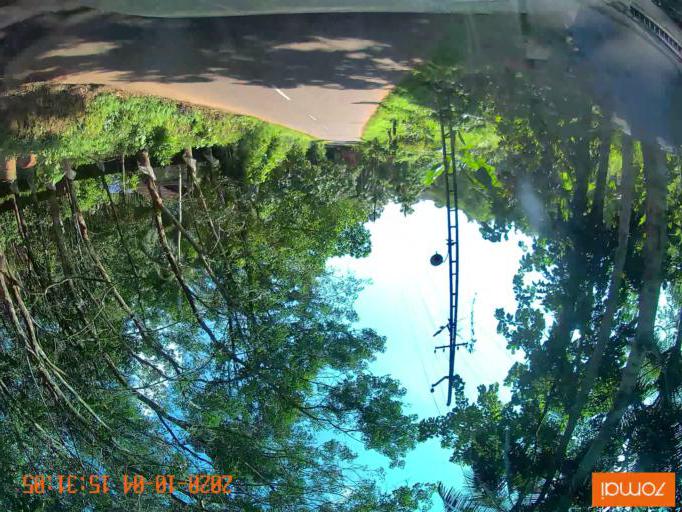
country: IN
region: Kerala
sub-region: Kottayam
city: Palackattumala
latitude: 9.7273
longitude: 76.6403
